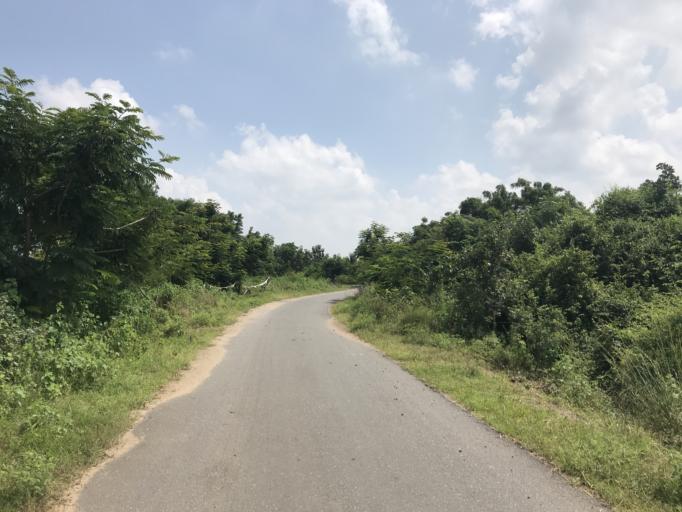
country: IN
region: Telangana
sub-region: Warangal
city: Mahbubabad
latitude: 17.6845
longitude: 79.7178
